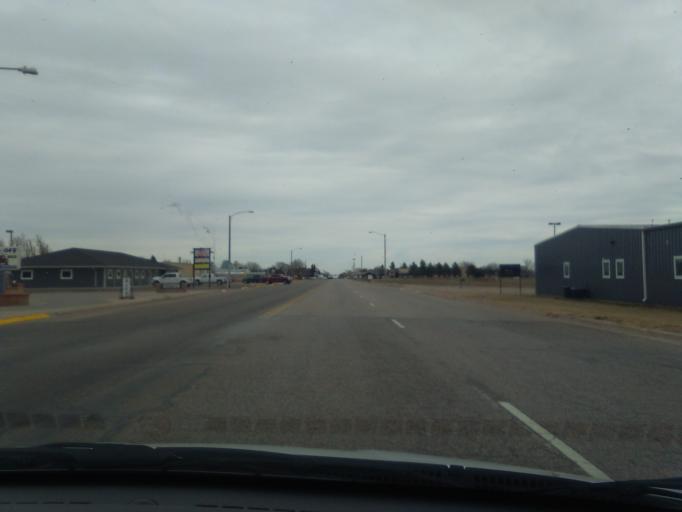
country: US
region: Colorado
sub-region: Yuma County
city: Yuma
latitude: 40.1184
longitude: -102.7364
